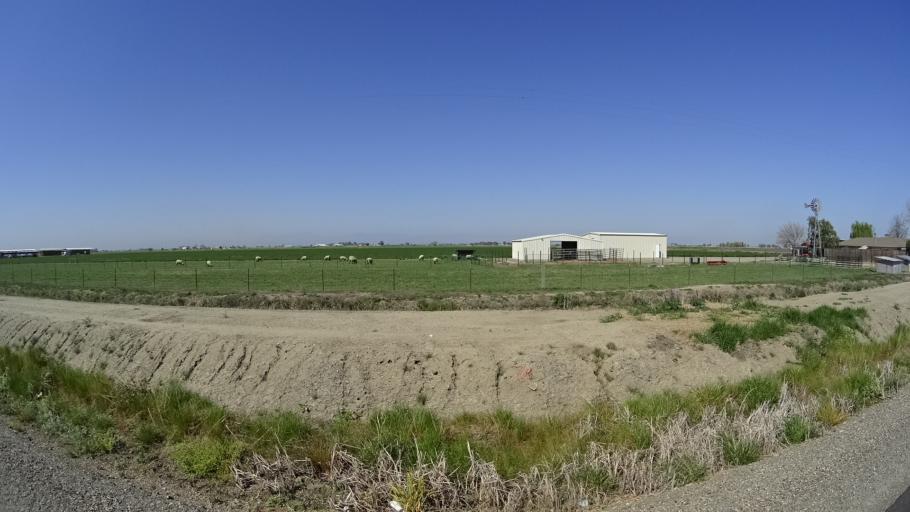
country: US
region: California
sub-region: Glenn County
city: Willows
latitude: 39.5779
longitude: -122.0652
